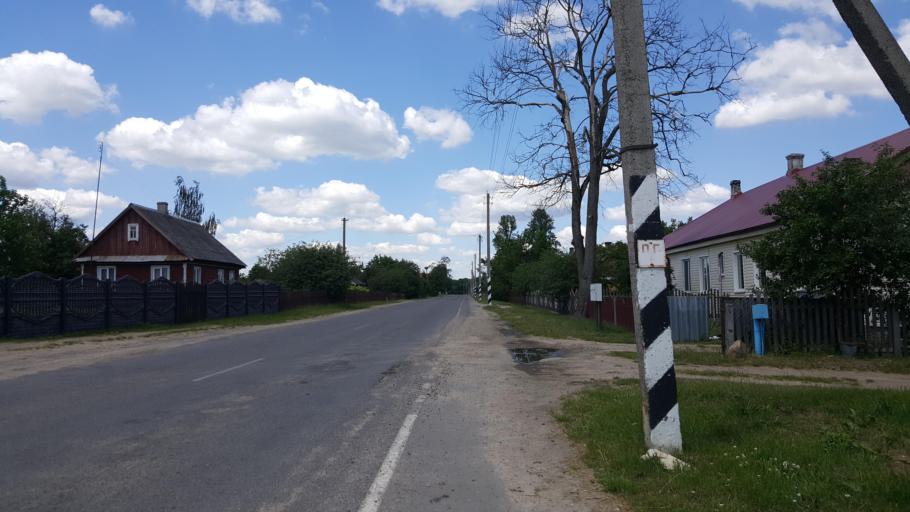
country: PL
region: Podlasie
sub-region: Powiat hajnowski
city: Czeremcha
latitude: 52.4718
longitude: 23.5098
